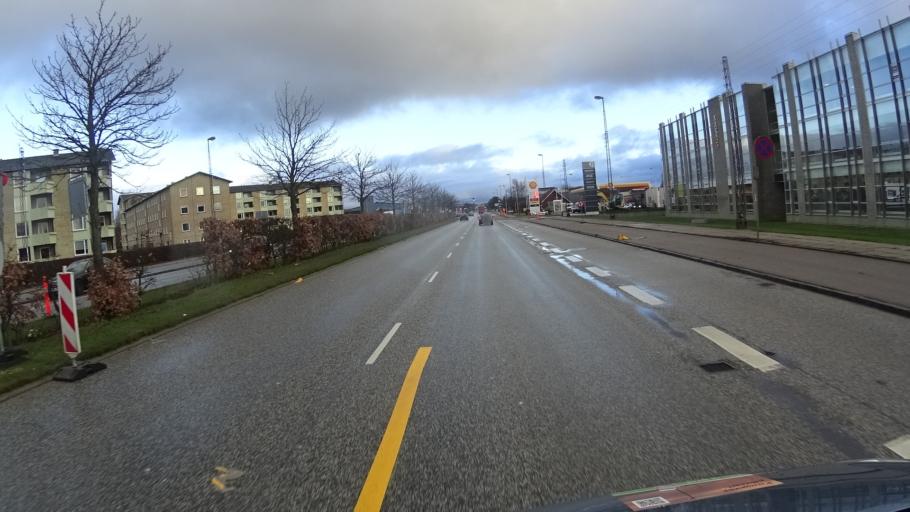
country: DK
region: South Denmark
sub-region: Vejle Kommune
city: Vejle
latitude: 55.7189
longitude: 9.5606
